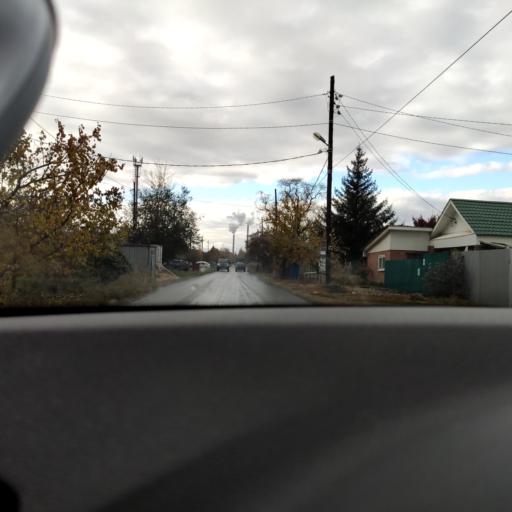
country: RU
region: Samara
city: Petra-Dubrava
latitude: 53.2484
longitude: 50.3274
